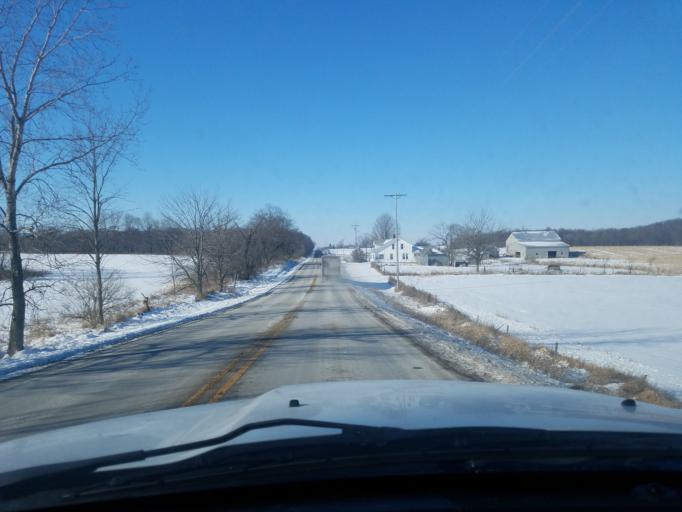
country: US
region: Indiana
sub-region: Noble County
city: Kendallville
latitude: 41.3949
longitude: -85.3094
